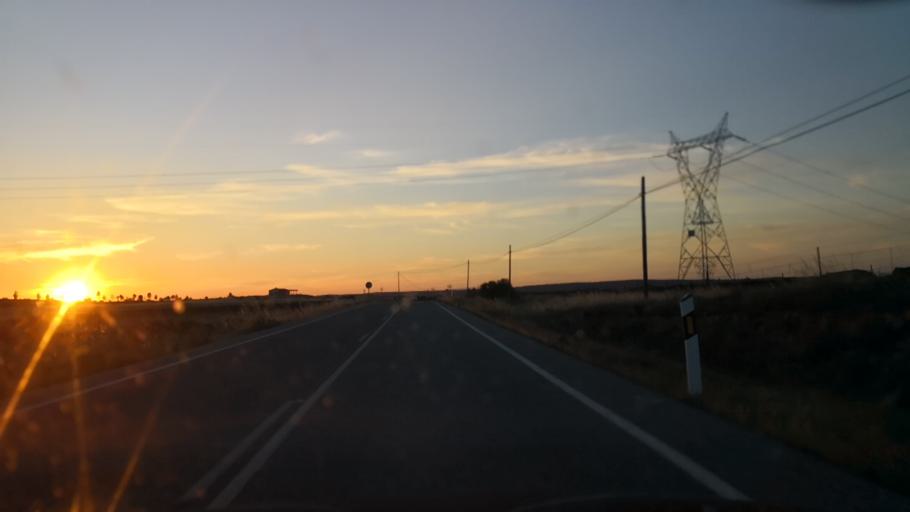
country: ES
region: Extremadura
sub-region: Provincia de Caceres
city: Alcantara
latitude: 39.6989
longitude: -6.8754
